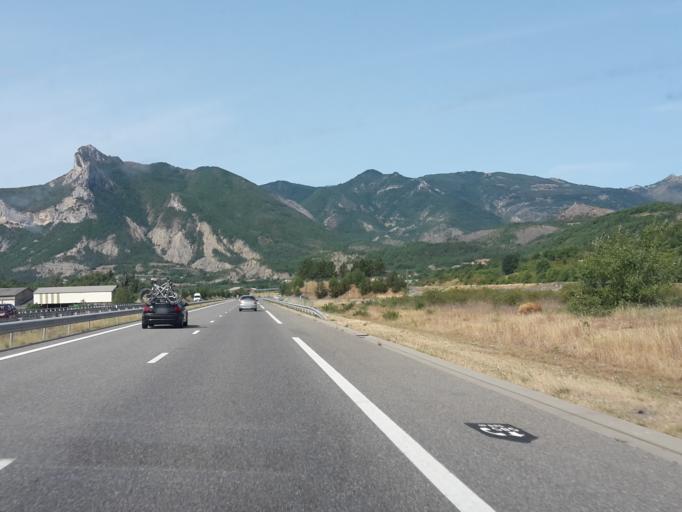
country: FR
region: Provence-Alpes-Cote d'Azur
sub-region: Departement des Hautes-Alpes
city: Tallard
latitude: 44.4184
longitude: 5.9855
